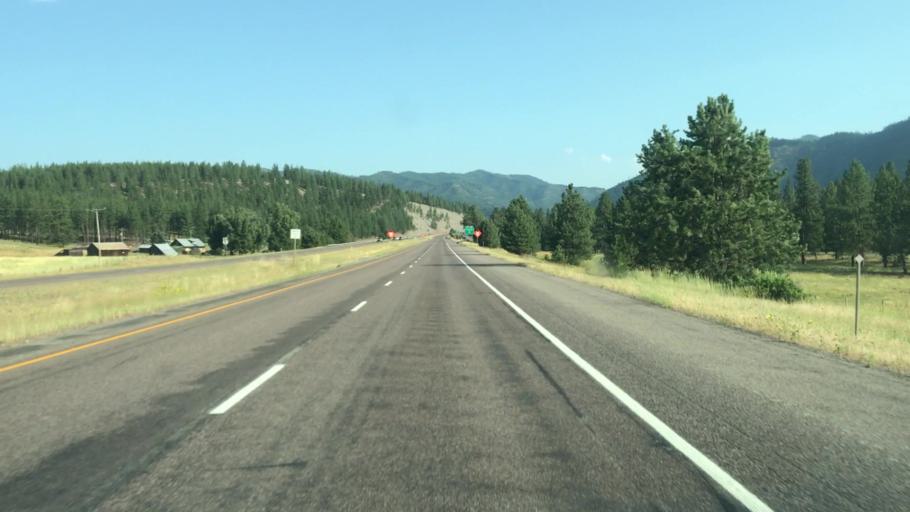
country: US
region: Montana
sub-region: Mineral County
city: Superior
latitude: 47.0311
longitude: -114.7429
